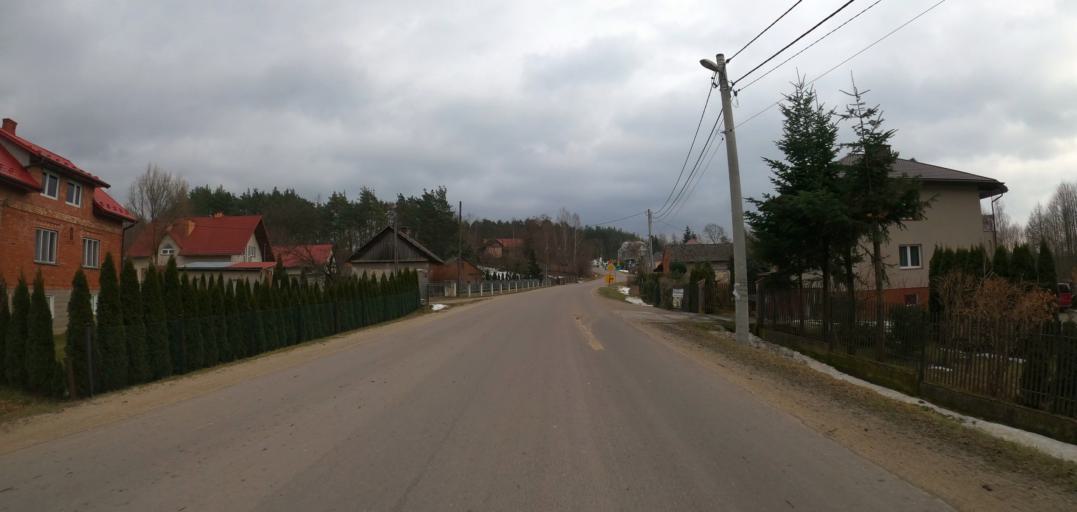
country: PL
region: Subcarpathian Voivodeship
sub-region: Powiat debicki
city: Pilzno
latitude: 49.9775
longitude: 21.3428
